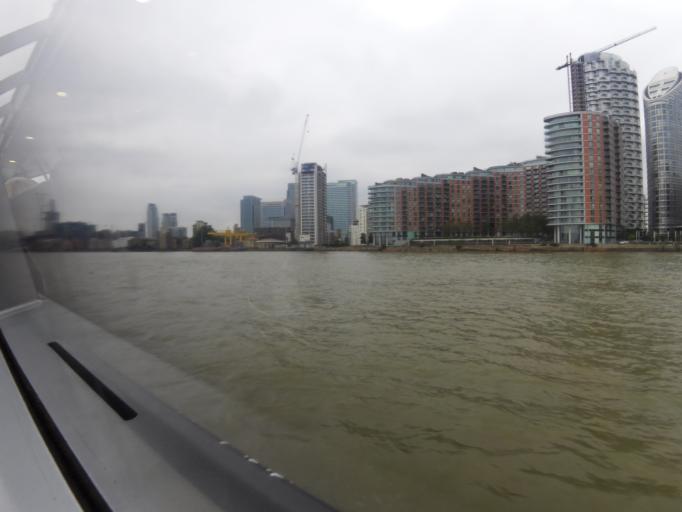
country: GB
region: England
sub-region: Greater London
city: Poplar
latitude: 51.5052
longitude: -0.0021
